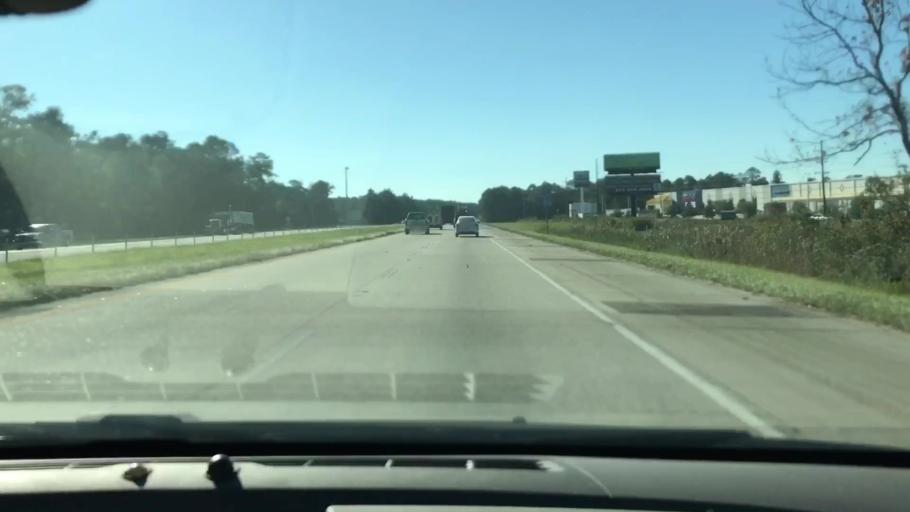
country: US
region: Louisiana
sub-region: Saint Tammany Parish
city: Pearl River
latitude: 30.3478
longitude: -89.7397
